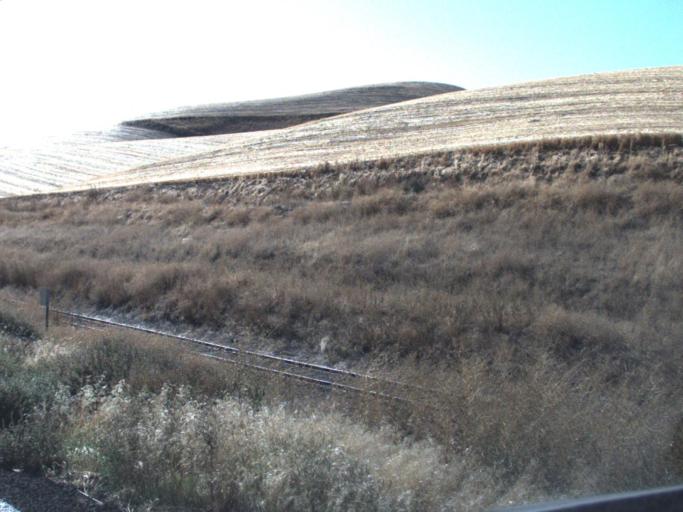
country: US
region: Washington
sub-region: Walla Walla County
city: Walla Walla
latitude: 46.2562
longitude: -118.3569
